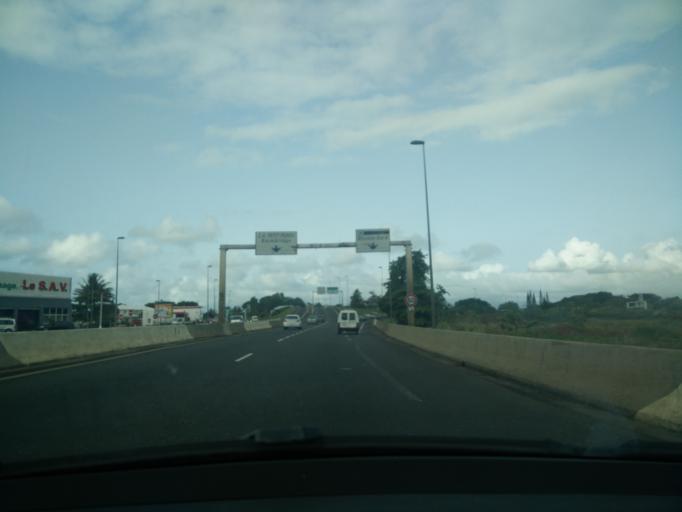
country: GP
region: Guadeloupe
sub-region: Guadeloupe
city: Les Abymes
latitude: 16.2721
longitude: -61.5110
